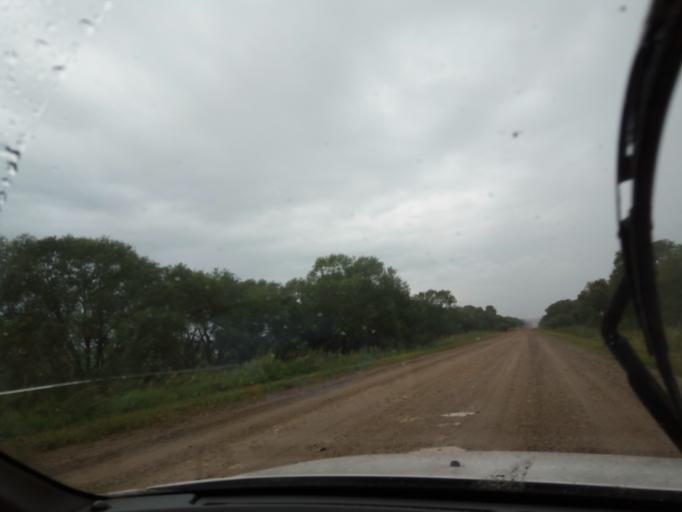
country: RU
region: Primorskiy
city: Lazo
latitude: 45.8406
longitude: 133.6437
